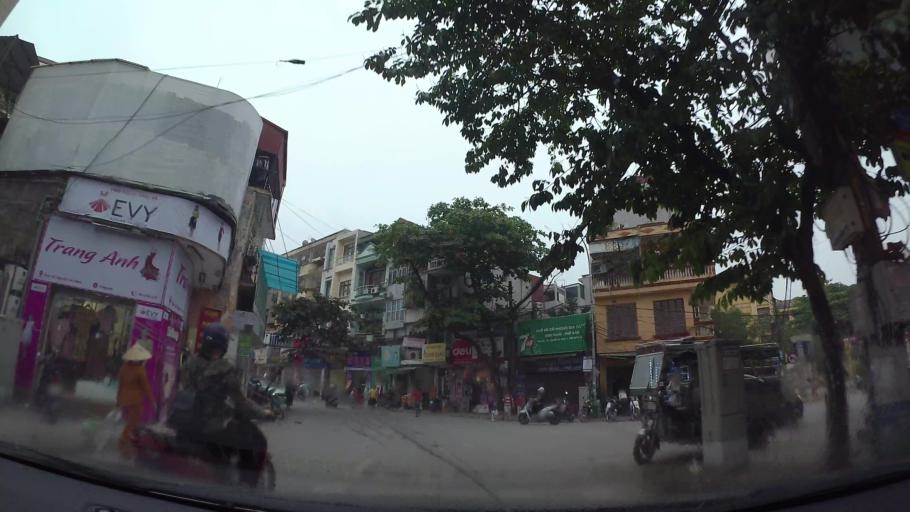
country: VN
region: Ha Noi
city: Hai BaTrung
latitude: 20.9892
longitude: 105.8459
